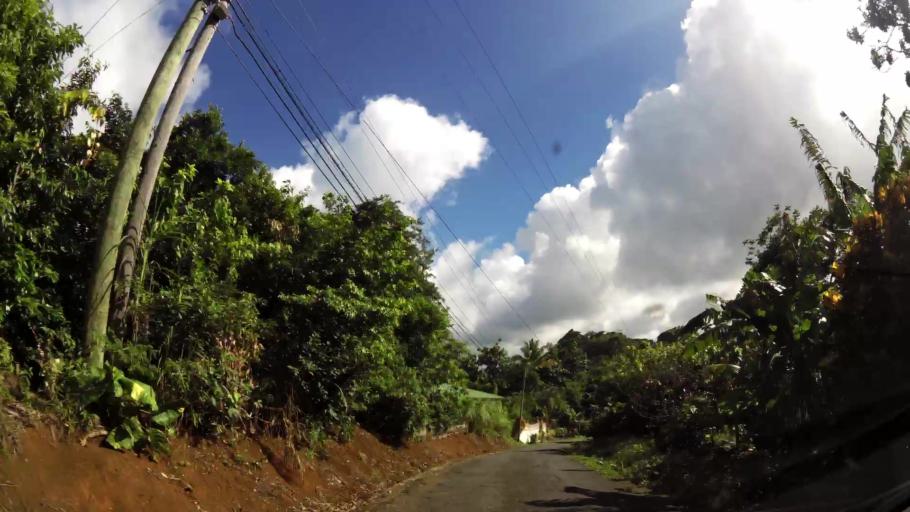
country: DM
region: Saint Andrew
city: Calibishie
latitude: 15.6060
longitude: -61.3999
